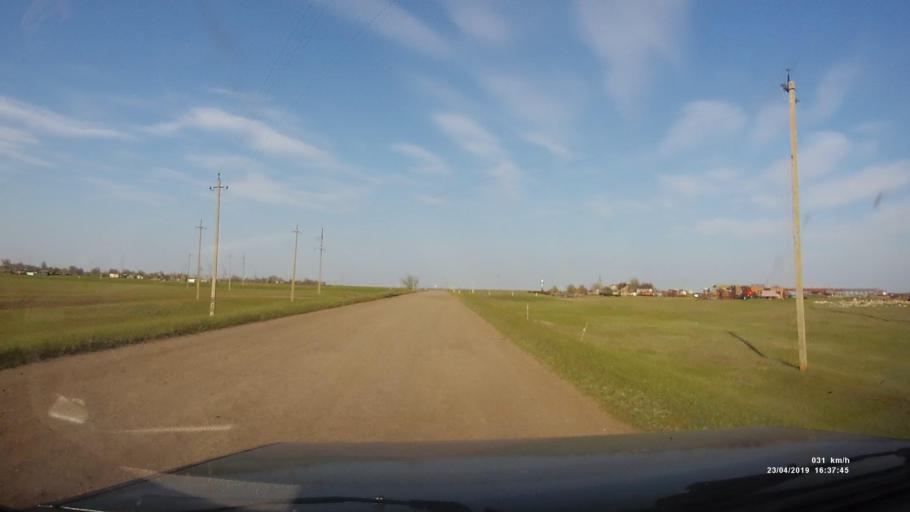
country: RU
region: Kalmykiya
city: Priyutnoye
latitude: 46.3334
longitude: 43.1489
